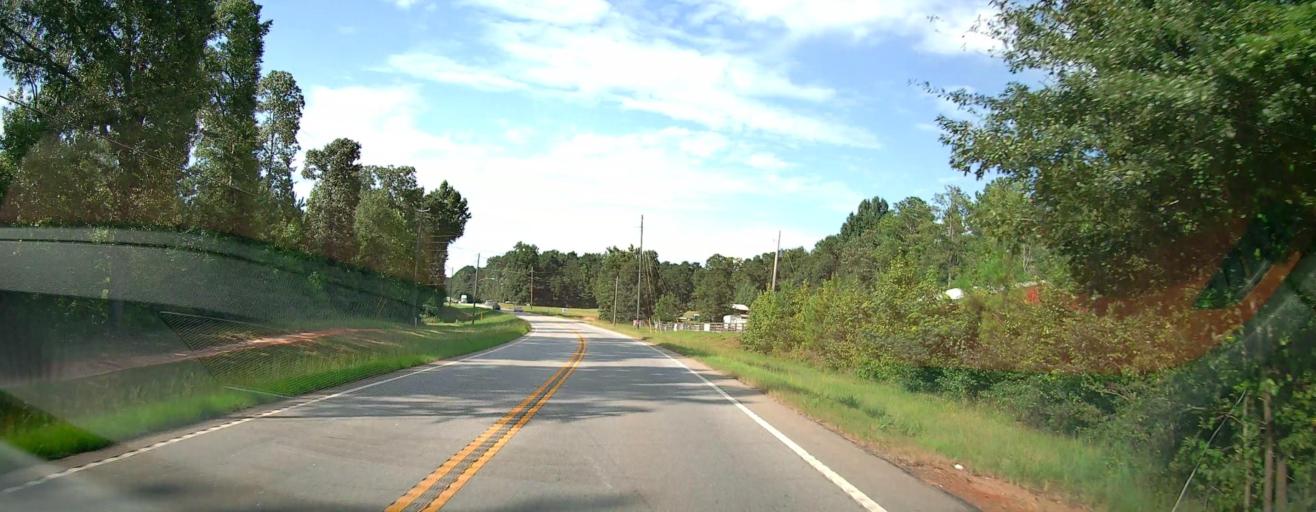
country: US
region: Georgia
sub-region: Coweta County
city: Senoia
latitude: 33.2308
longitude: -84.5670
